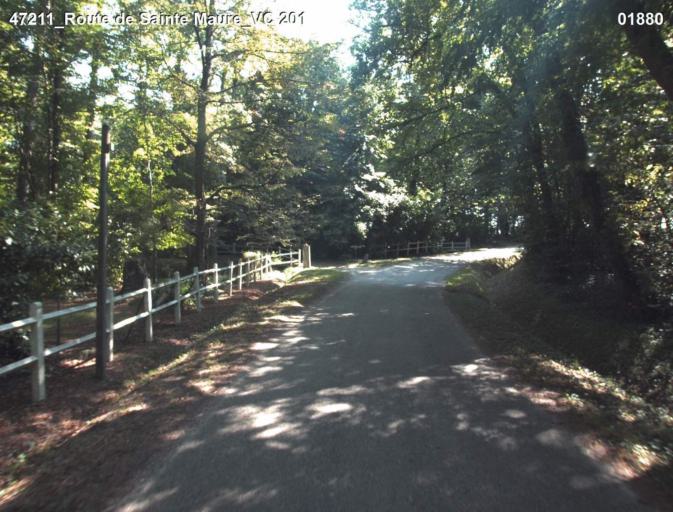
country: FR
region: Aquitaine
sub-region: Departement du Lot-et-Garonne
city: Mezin
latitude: 44.0288
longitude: 0.1848
